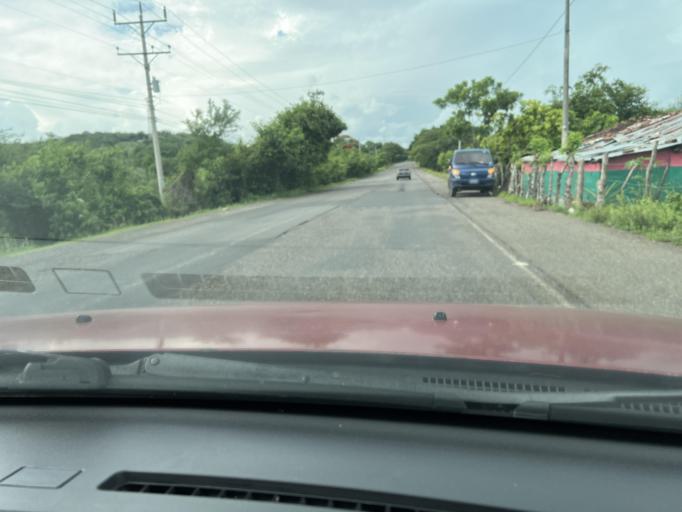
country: SV
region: La Union
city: San Alejo
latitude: 13.3938
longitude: -87.9008
